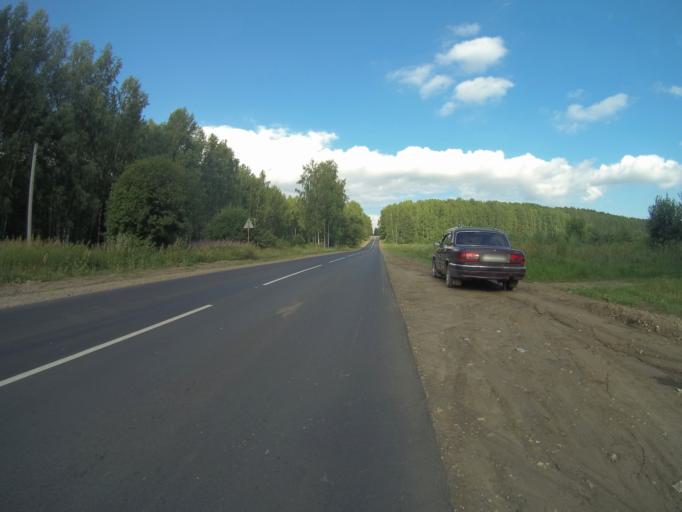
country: RU
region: Vladimir
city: Raduzhnyy
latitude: 56.0020
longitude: 40.2743
